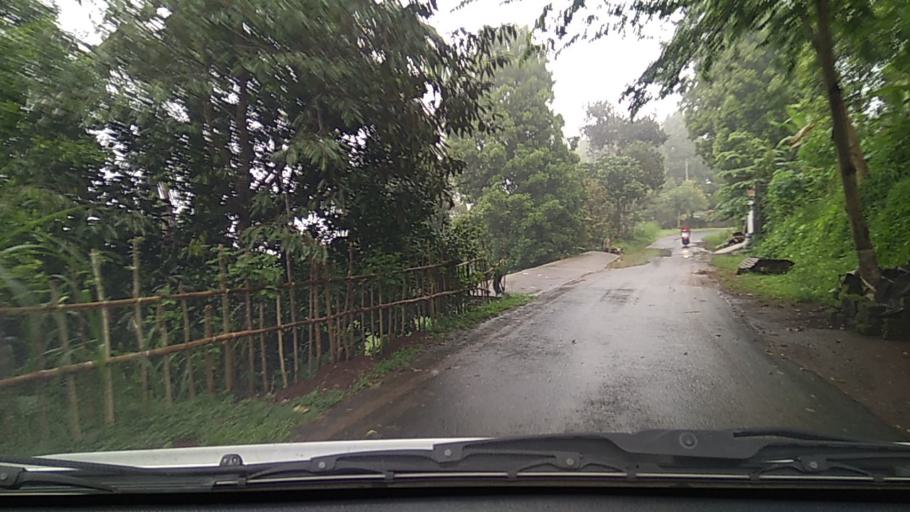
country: ID
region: Bali
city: Banjar Ambengan
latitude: -8.1965
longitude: 115.1816
